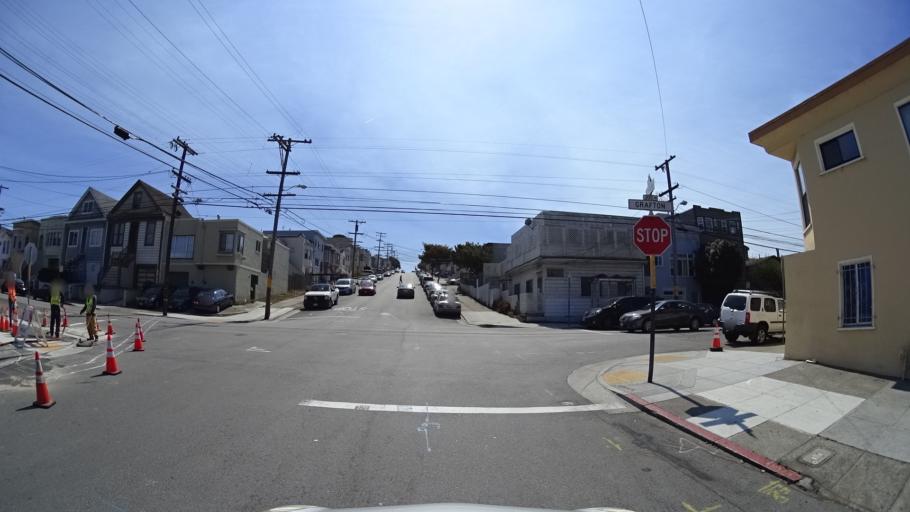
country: US
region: California
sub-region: San Mateo County
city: Daly City
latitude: 37.7202
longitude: -122.4562
